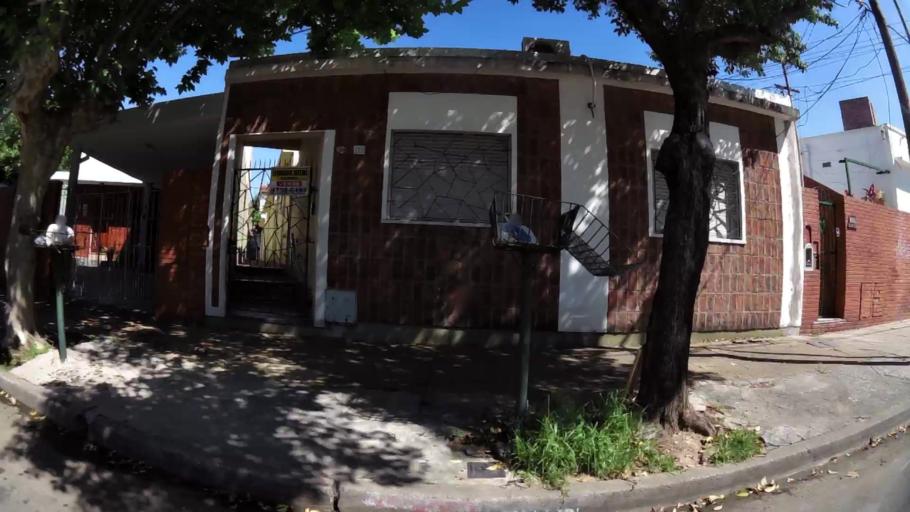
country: AR
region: Buenos Aires
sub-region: Partido de General San Martin
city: General San Martin
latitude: -34.5499
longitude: -58.5662
